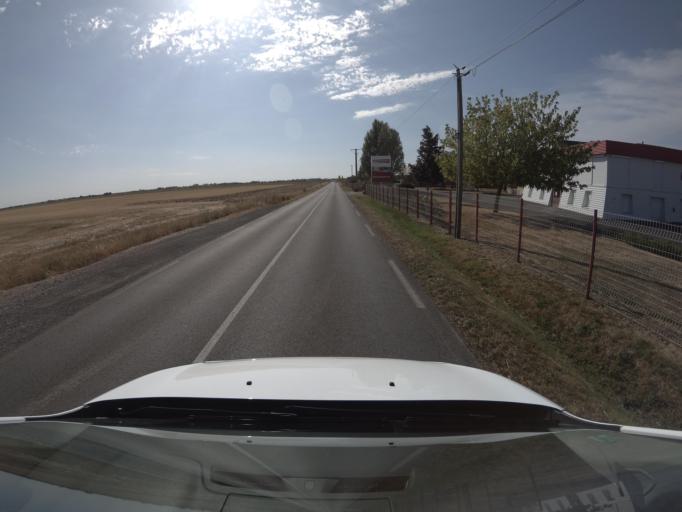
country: FR
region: Poitou-Charentes
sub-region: Departement des Deux-Sevres
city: Mauze-Thouarsais
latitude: 46.9988
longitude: -0.2879
